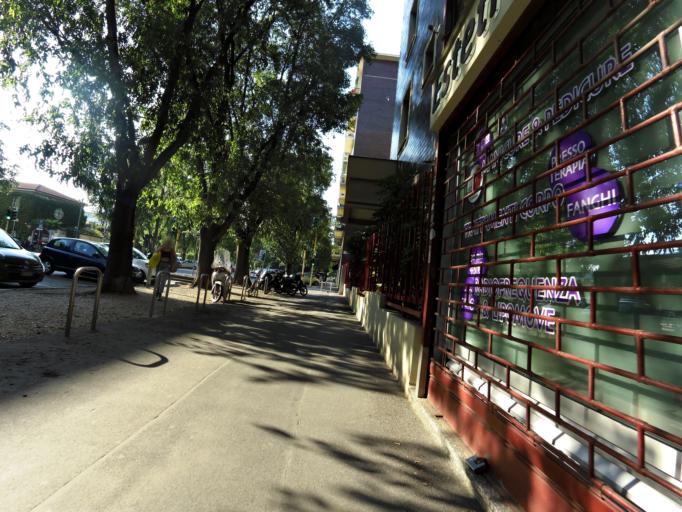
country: IT
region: Lombardy
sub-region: Citta metropolitana di Milano
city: Milano
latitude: 45.4539
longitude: 9.1639
